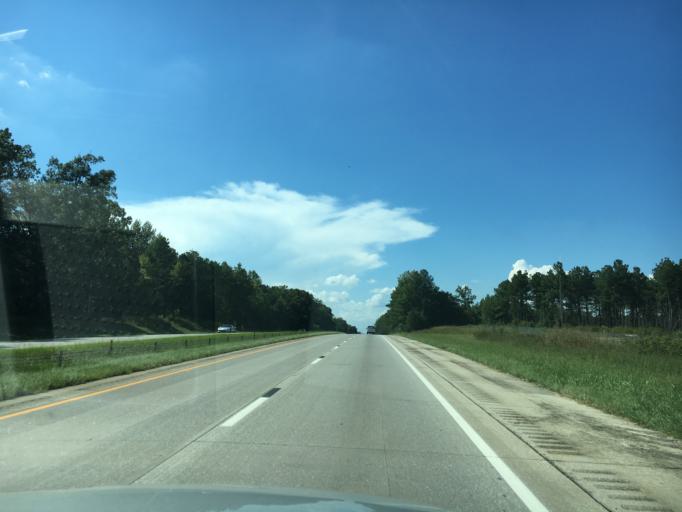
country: US
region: South Carolina
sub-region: Laurens County
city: Watts Mills
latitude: 34.5752
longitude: -82.0358
